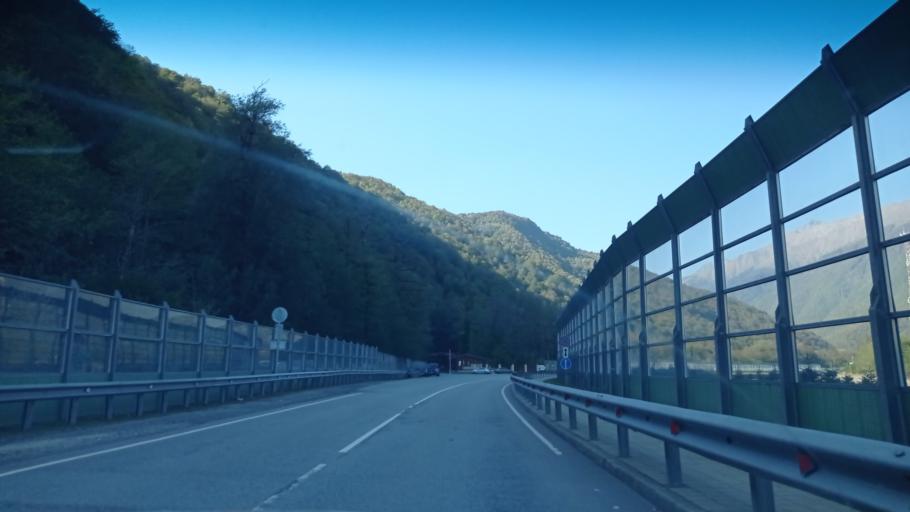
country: RU
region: Krasnodarskiy
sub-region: Sochi City
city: Krasnaya Polyana
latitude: 43.6908
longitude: 40.2724
